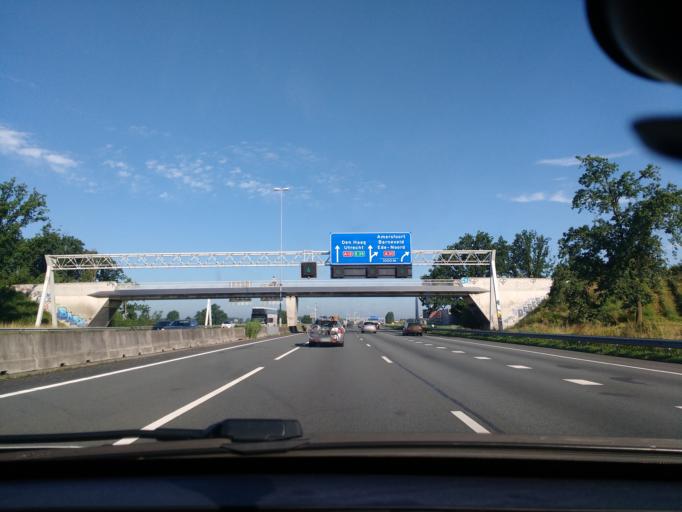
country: NL
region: Gelderland
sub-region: Gemeente Ede
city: Ede
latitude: 52.0182
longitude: 5.6328
